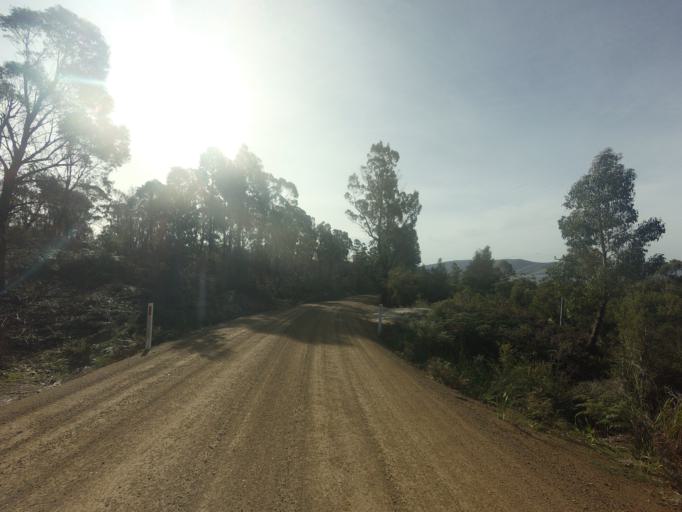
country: AU
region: Tasmania
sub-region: Kingborough
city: Kettering
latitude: -43.0807
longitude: 147.2634
